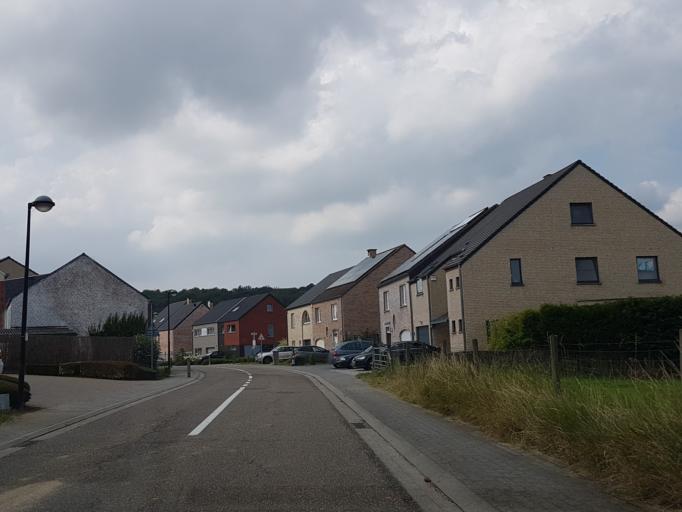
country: BE
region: Flanders
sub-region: Provincie Vlaams-Brabant
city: Kortenberg
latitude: 50.8768
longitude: 4.5531
